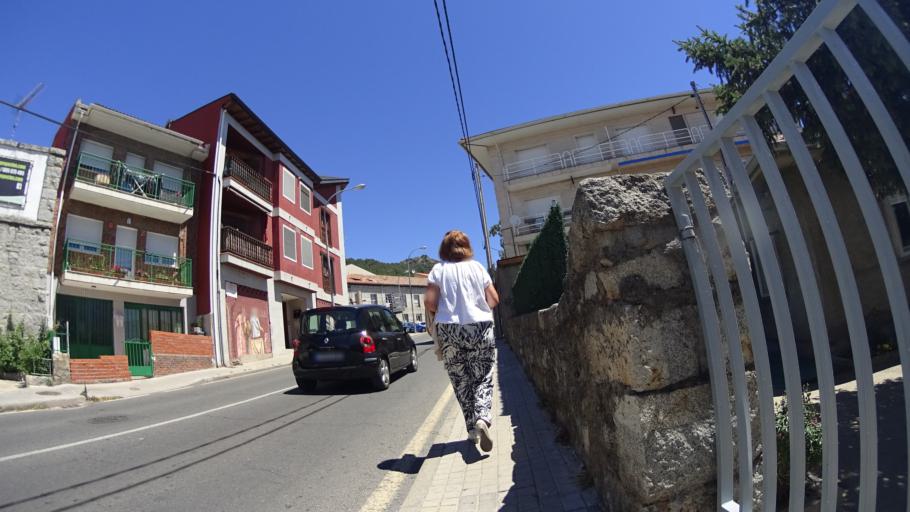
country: ES
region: Madrid
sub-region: Provincia de Madrid
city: Collado Mediano
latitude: 40.6924
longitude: -4.0270
